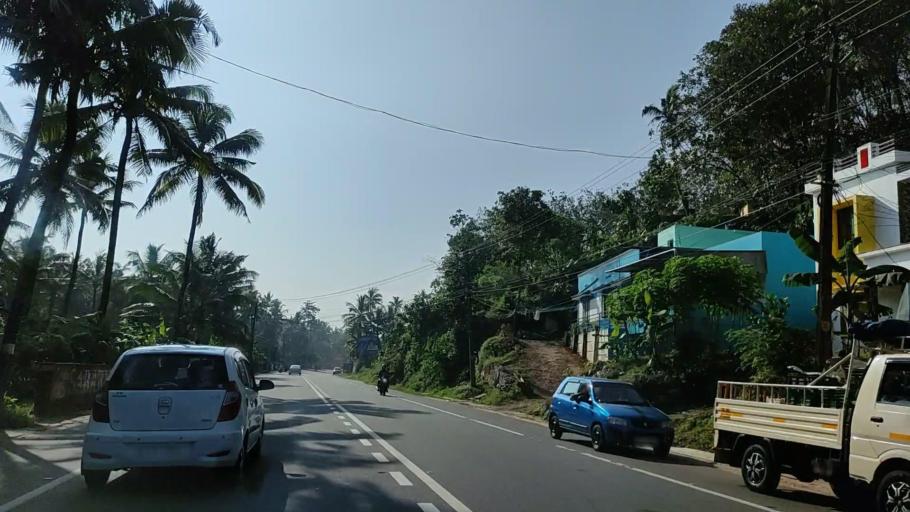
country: IN
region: Kerala
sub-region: Kollam
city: Punalur
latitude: 8.9210
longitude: 76.8545
